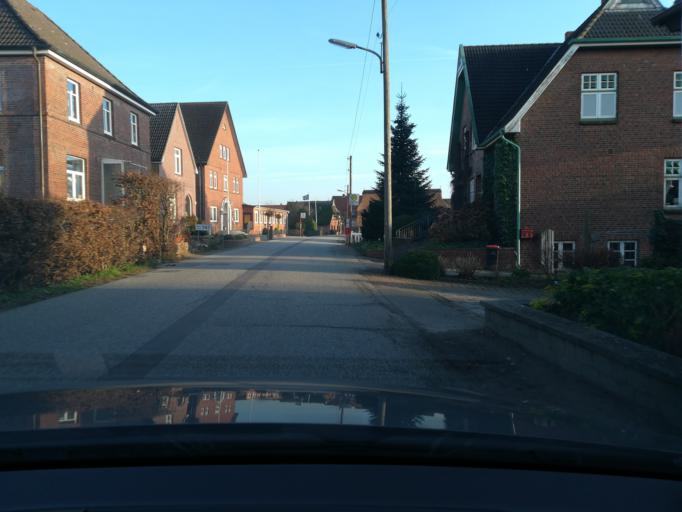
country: DE
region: Hamburg
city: Bergedorf
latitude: 53.4377
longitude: 10.1964
